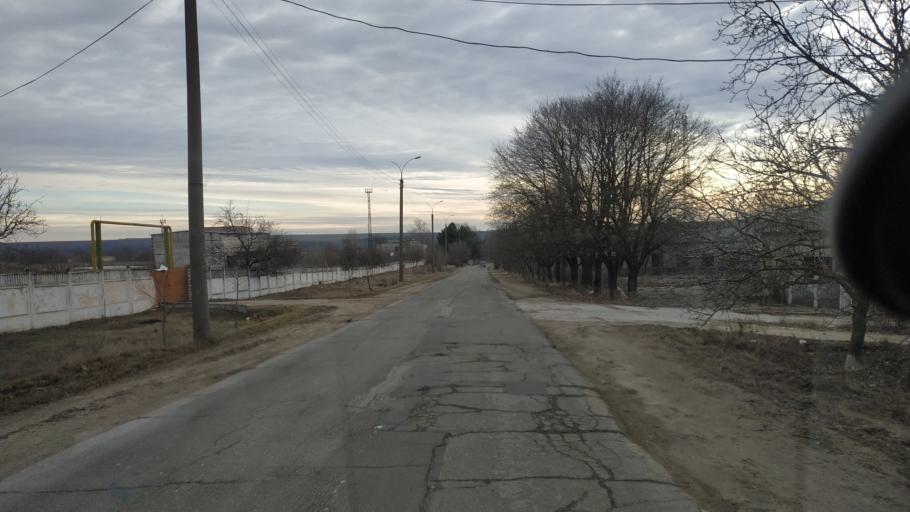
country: MD
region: Criuleni
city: Criuleni
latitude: 47.2218
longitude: 29.1521
